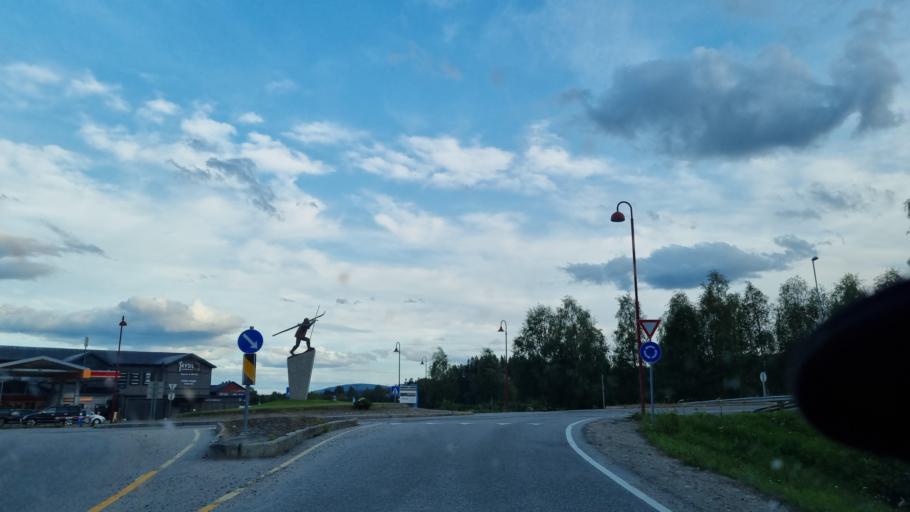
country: NO
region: Hedmark
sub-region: Trysil
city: Innbygda
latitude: 61.3166
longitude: 12.2599
